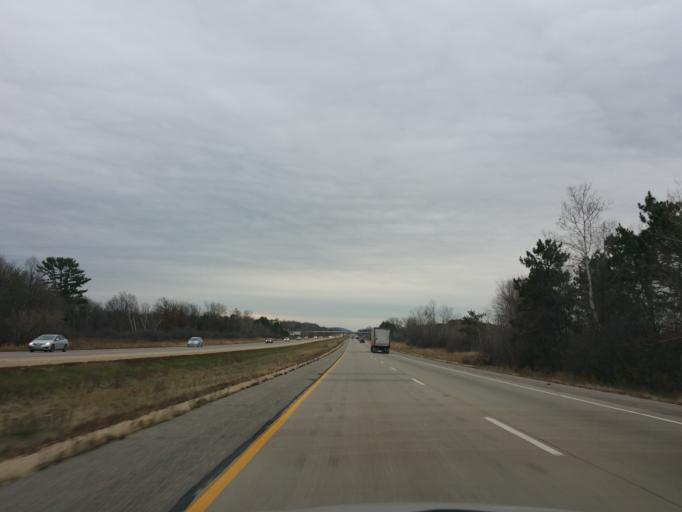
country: US
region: Wisconsin
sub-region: Juneau County
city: Mauston
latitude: 43.8183
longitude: -90.0791
